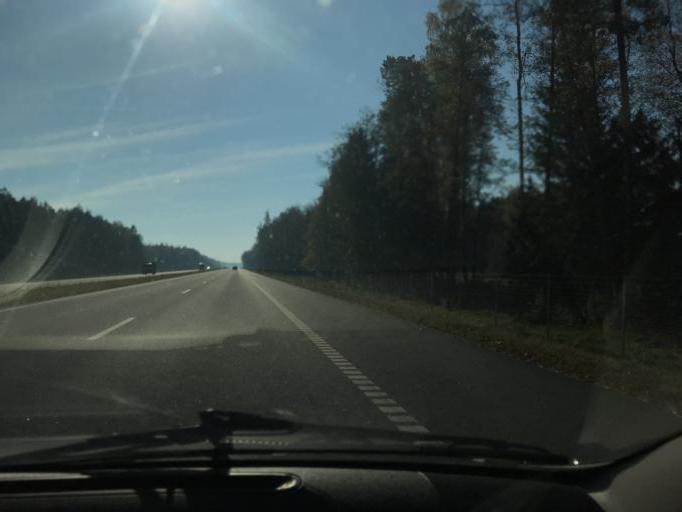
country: BY
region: Minsk
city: Slutsk
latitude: 53.3101
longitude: 27.5391
